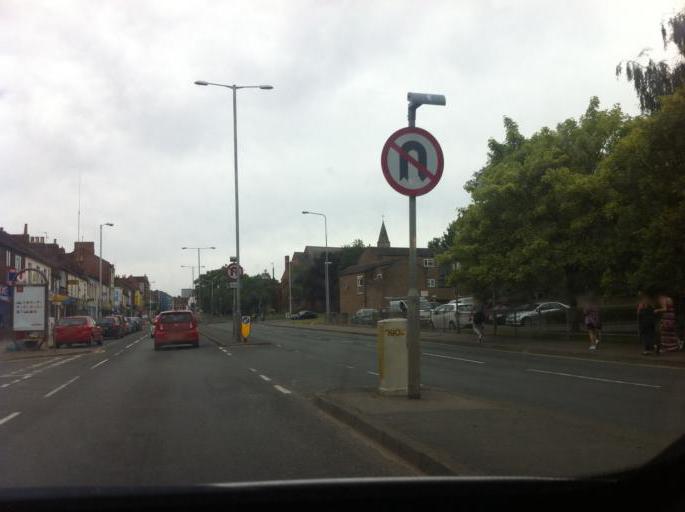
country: GB
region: England
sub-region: Northamptonshire
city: Northampton
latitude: 52.2411
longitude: -0.8838
